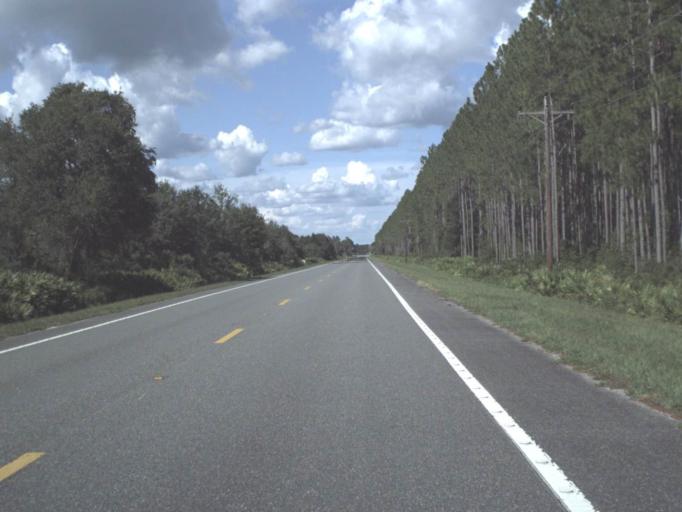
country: US
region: Florida
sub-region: Taylor County
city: Steinhatchee
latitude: 29.7702
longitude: -83.3356
